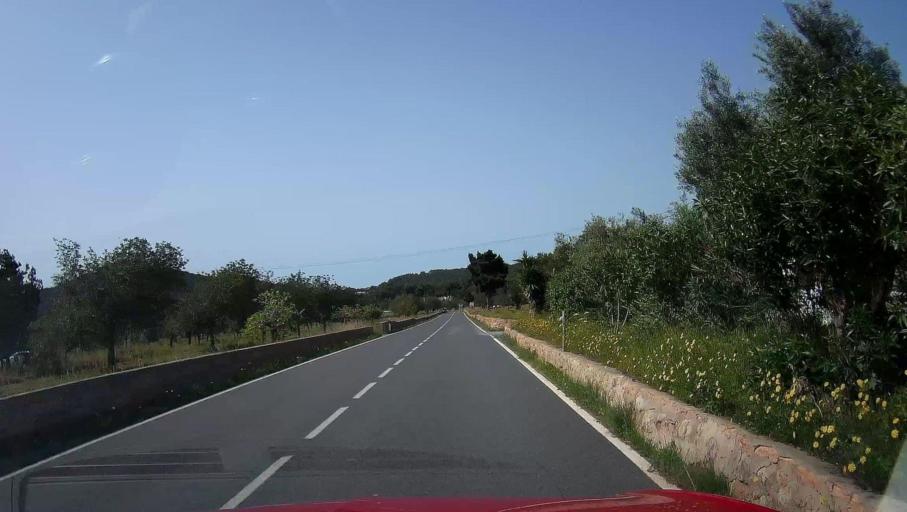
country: ES
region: Balearic Islands
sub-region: Illes Balears
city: Sant Joan de Labritja
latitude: 39.0515
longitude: 1.5735
